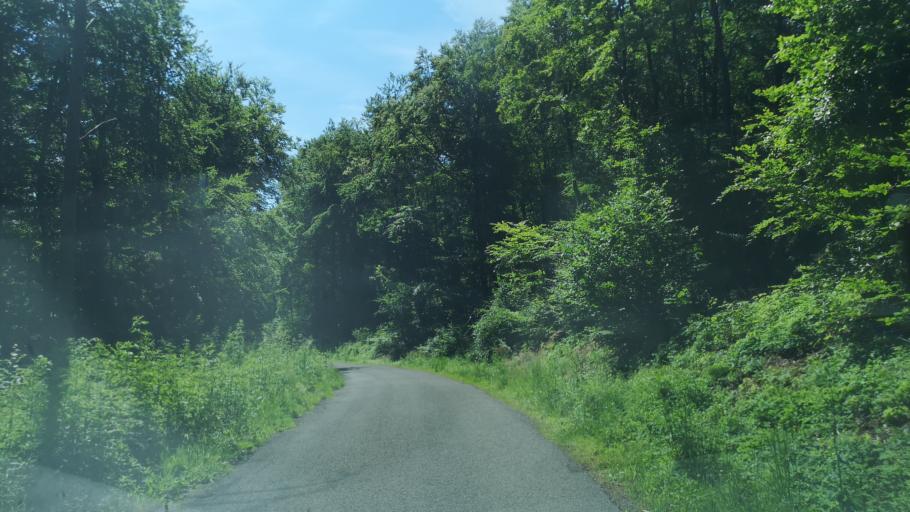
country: FR
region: Lorraine
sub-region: Departement de la Meuse
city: Vigneulles-les-Hattonchatel
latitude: 49.0309
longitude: 5.6453
